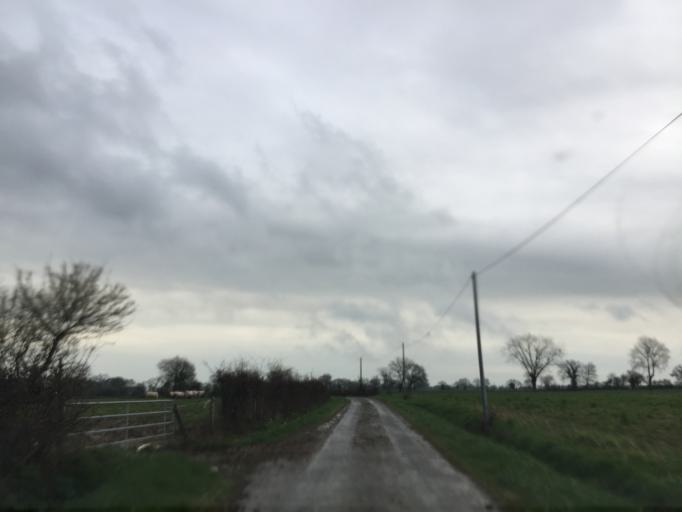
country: FR
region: Pays de la Loire
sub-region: Departement de la Loire-Atlantique
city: Soudan
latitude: 47.7531
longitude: -1.2963
